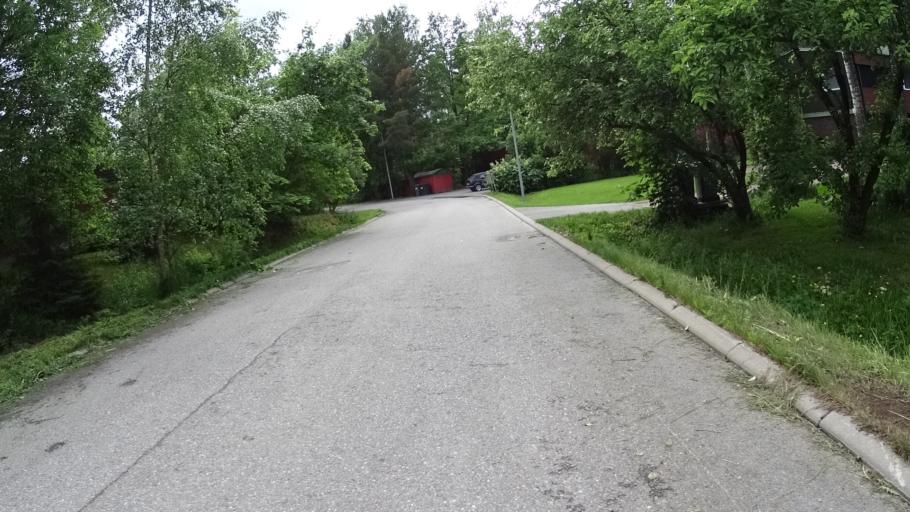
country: FI
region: Uusimaa
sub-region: Helsinki
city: Kilo
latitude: 60.2505
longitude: 24.8126
